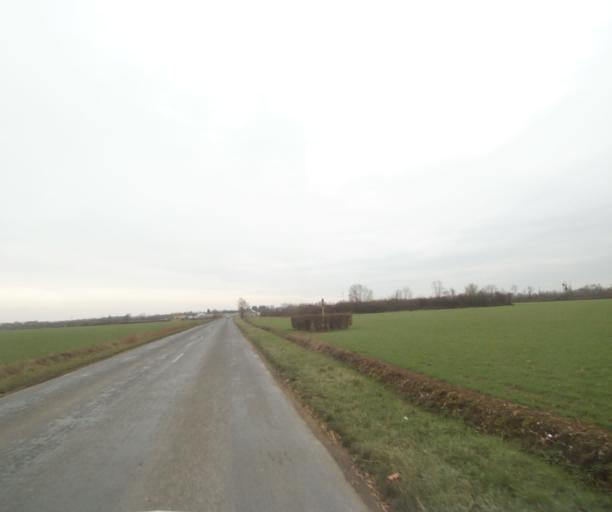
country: FR
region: Champagne-Ardenne
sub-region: Departement de la Haute-Marne
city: Villiers-en-Lieu
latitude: 48.6626
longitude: 4.9069
